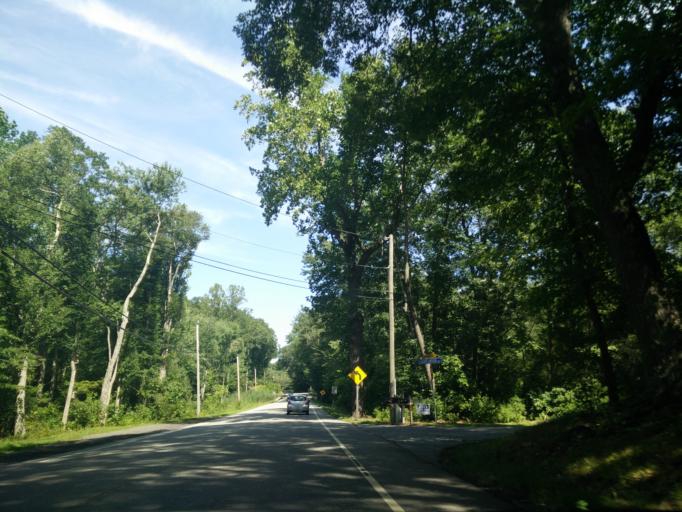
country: US
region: Connecticut
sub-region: Middlesex County
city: Clinton
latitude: 41.3122
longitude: -72.5394
